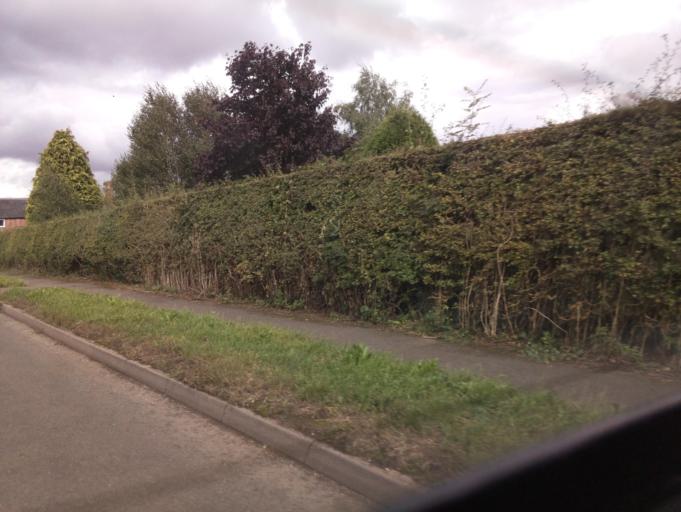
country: GB
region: England
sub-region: Staffordshire
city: Eccleshall
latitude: 52.8718
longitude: -2.2479
